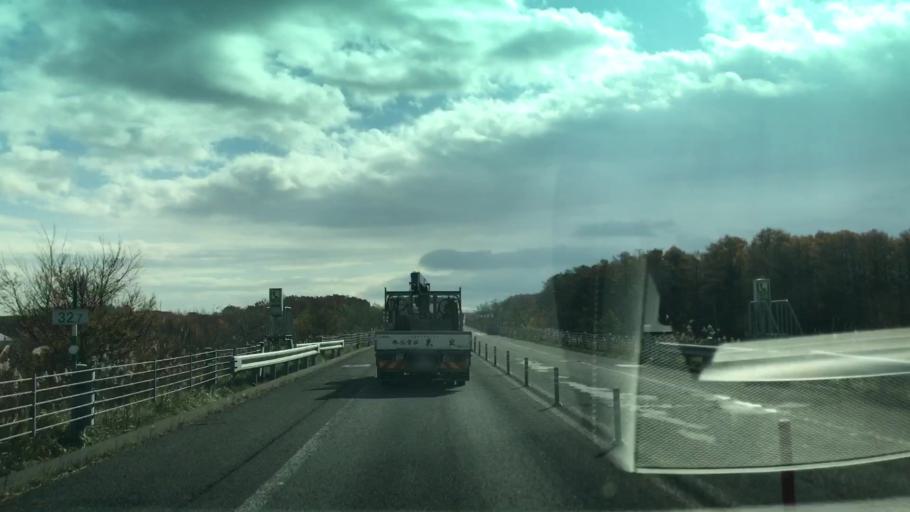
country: JP
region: Hokkaido
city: Tomakomai
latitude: 42.5701
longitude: 141.9756
